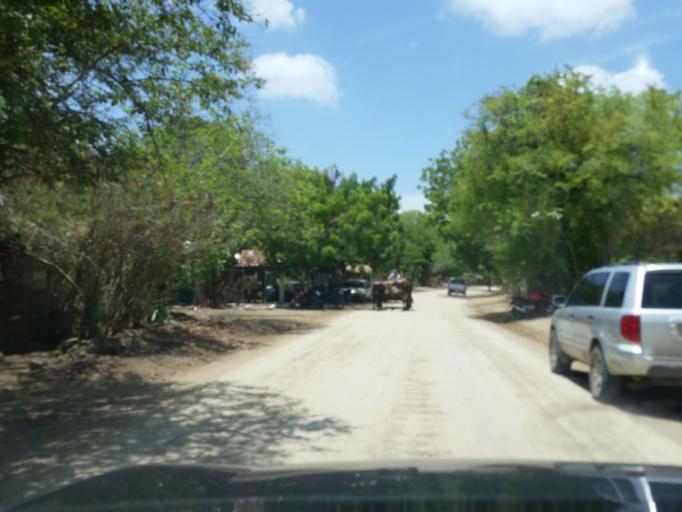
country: NI
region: Rivas
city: Tola
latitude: 11.4597
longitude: -86.0791
